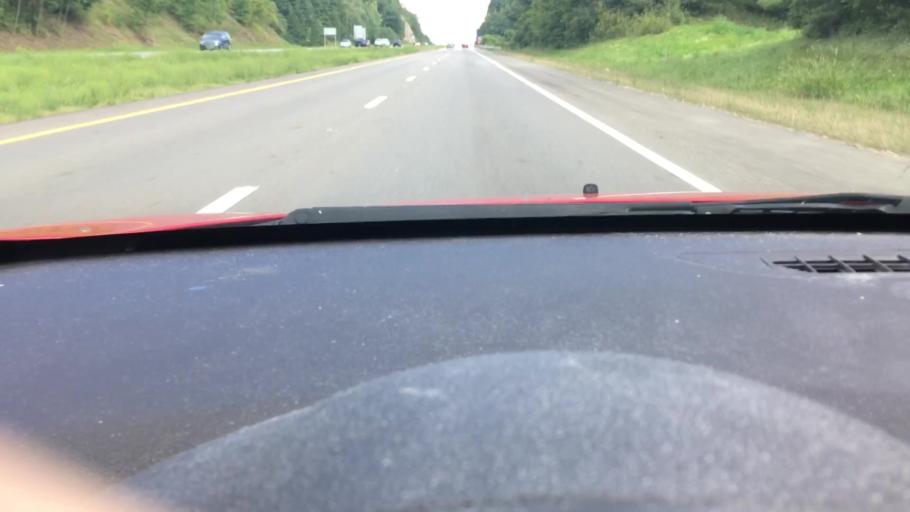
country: US
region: Ohio
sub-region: Athens County
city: Athens
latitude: 39.3569
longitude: -82.0996
